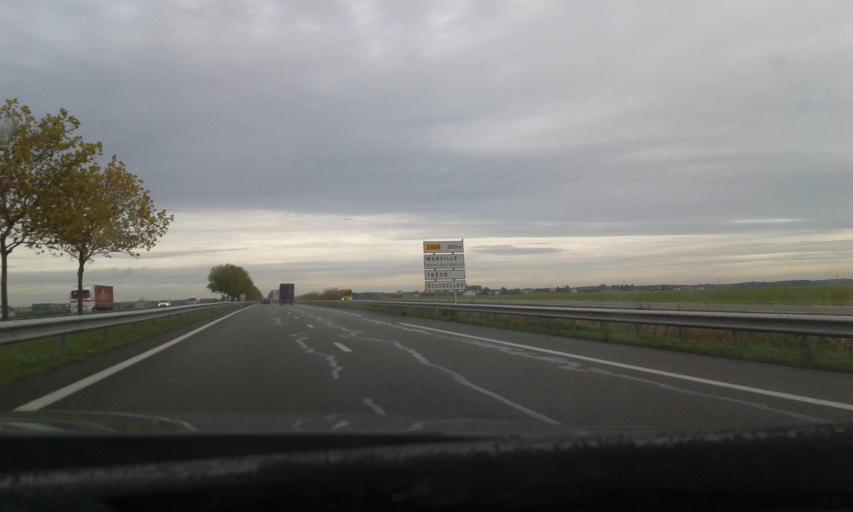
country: FR
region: Centre
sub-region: Departement d'Eure-et-Loir
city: Luray
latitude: 48.6624
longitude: 1.3932
